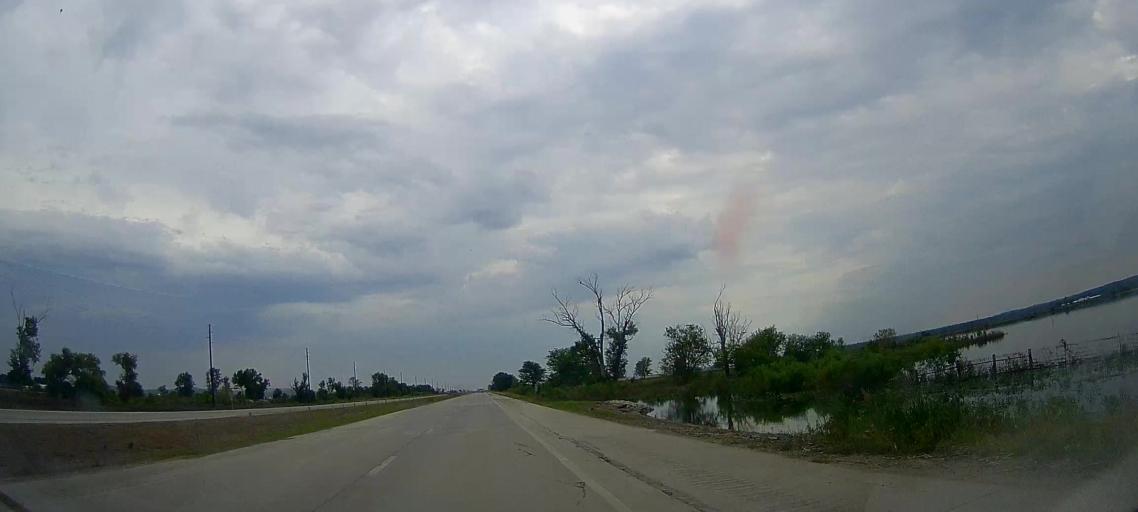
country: US
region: Iowa
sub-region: Pottawattamie County
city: Carter Lake
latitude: 41.3992
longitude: -95.8997
